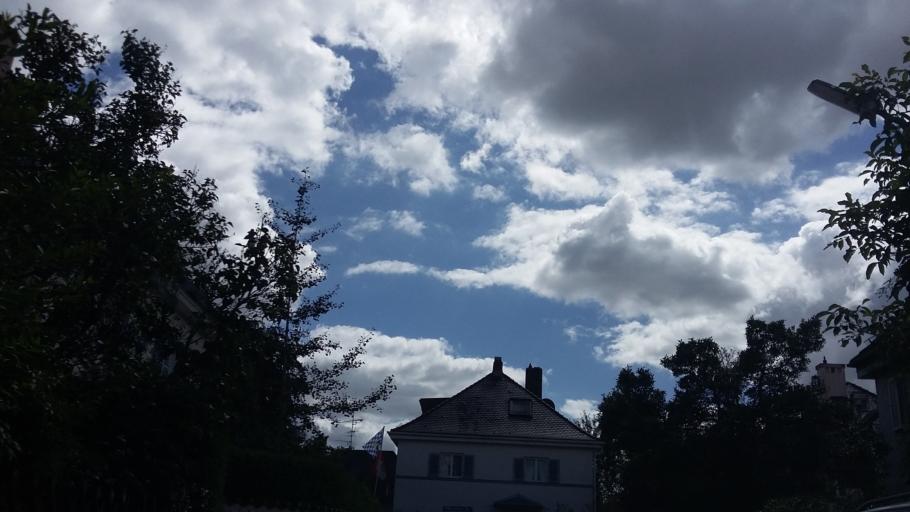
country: DE
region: Bavaria
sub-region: Upper Bavaria
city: Grafelfing
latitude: 48.1445
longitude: 11.4218
